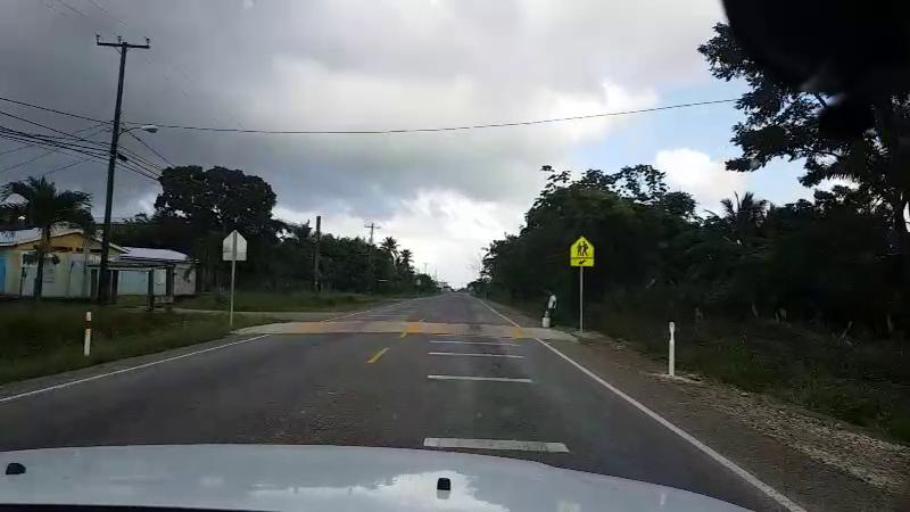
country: BZ
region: Stann Creek
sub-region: Dangriga
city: Dangriga
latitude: 16.9926
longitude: -88.3757
